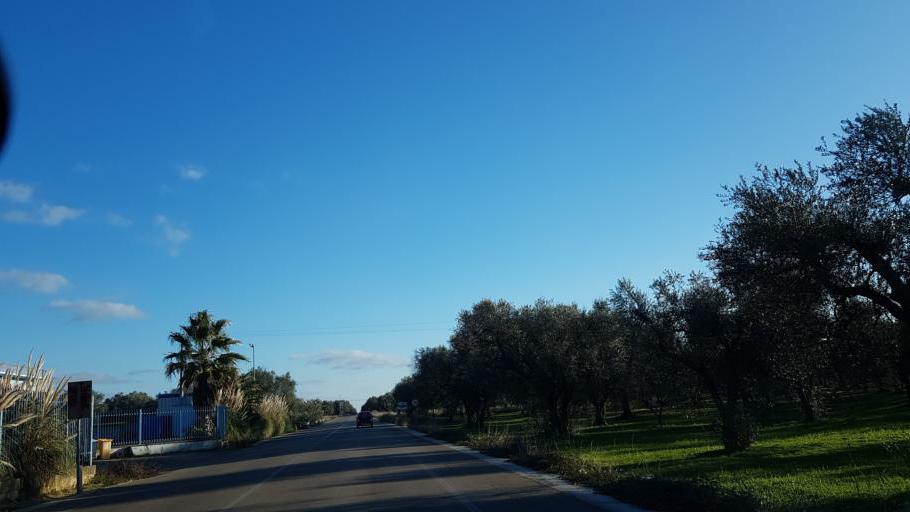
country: IT
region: Apulia
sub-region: Provincia di Brindisi
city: San Pietro Vernotico
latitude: 40.4741
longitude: 18.0101
